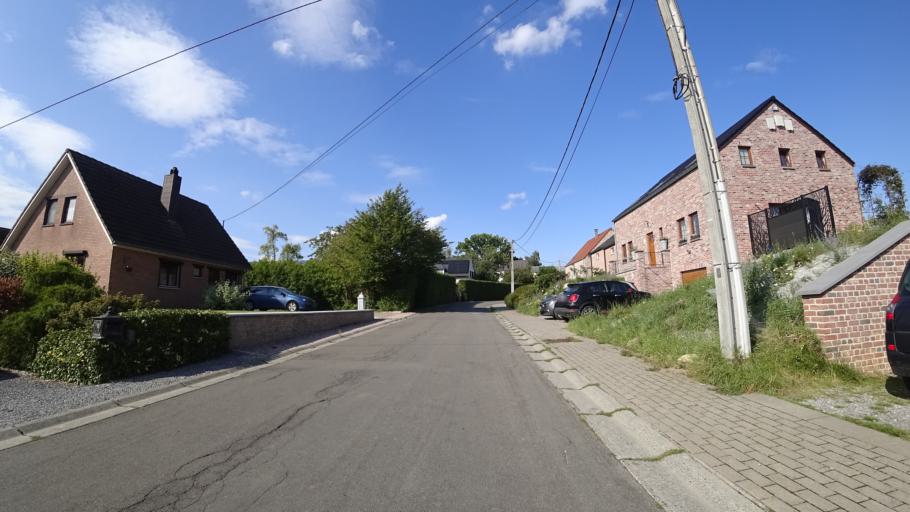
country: BE
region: Wallonia
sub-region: Province de Namur
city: Gembloux
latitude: 50.5351
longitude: 4.6587
